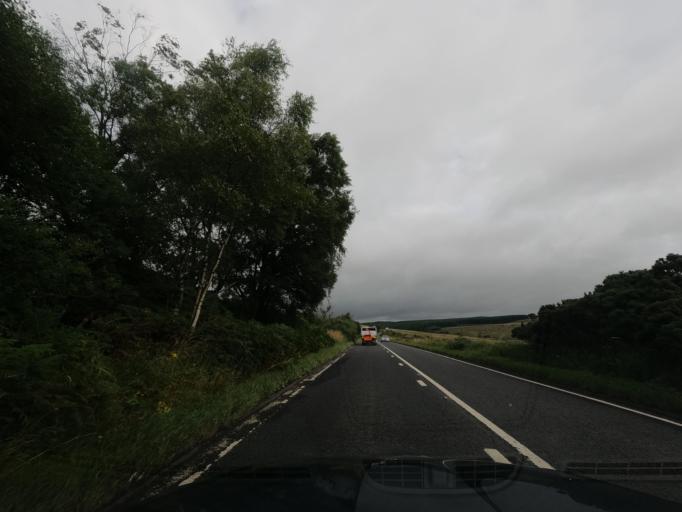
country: GB
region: England
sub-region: Northumberland
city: Whittingham
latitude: 55.3339
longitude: -1.8159
